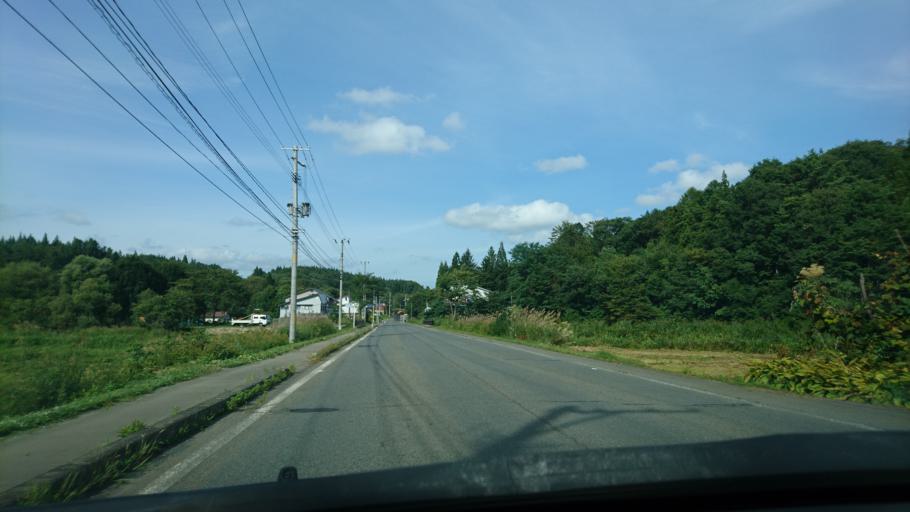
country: JP
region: Akita
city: Yokotemachi
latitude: 39.2977
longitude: 140.7346
